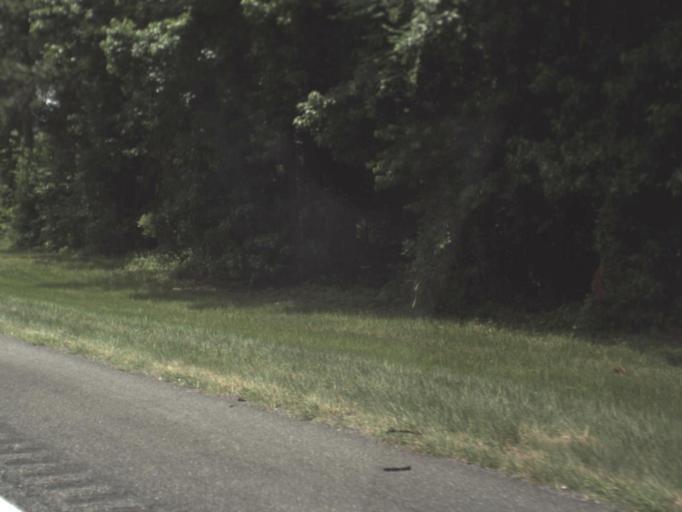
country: US
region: Florida
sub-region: Suwannee County
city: Wellborn
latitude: 30.2461
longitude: -82.7430
